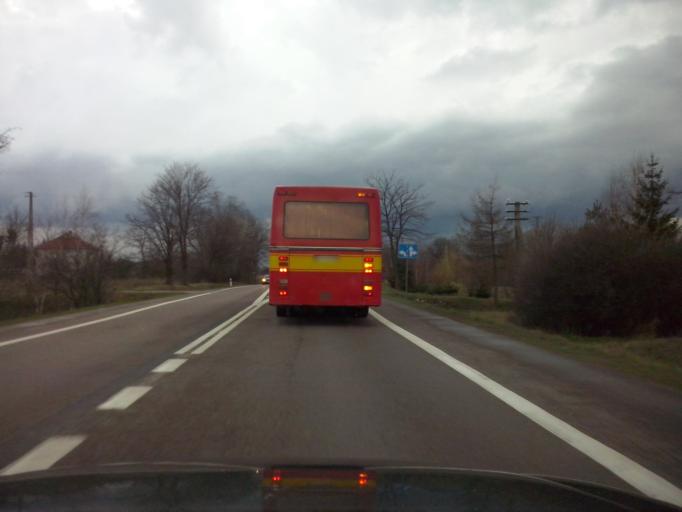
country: PL
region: Lublin Voivodeship
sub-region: Powiat chelmski
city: Rejowiec Fabryczny
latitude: 51.1740
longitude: 23.2702
